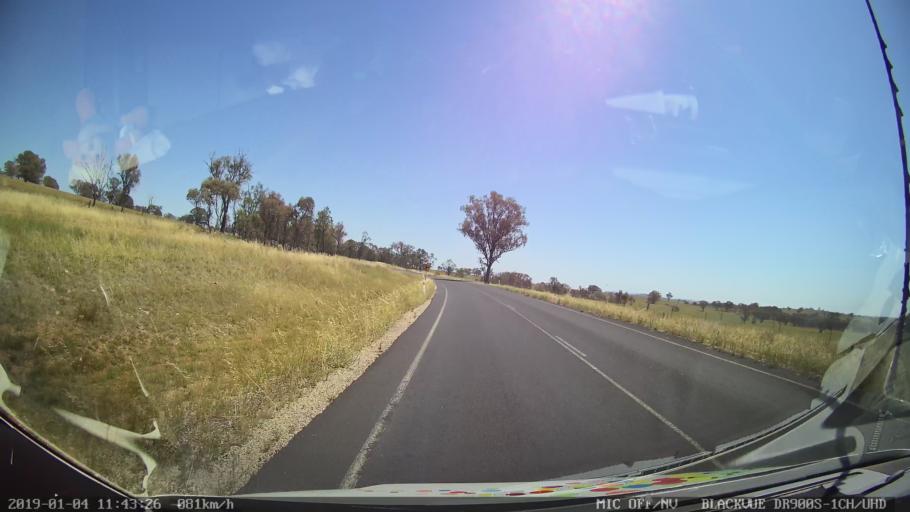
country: AU
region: New South Wales
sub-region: Cabonne
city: Molong
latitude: -32.9689
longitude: 148.7839
